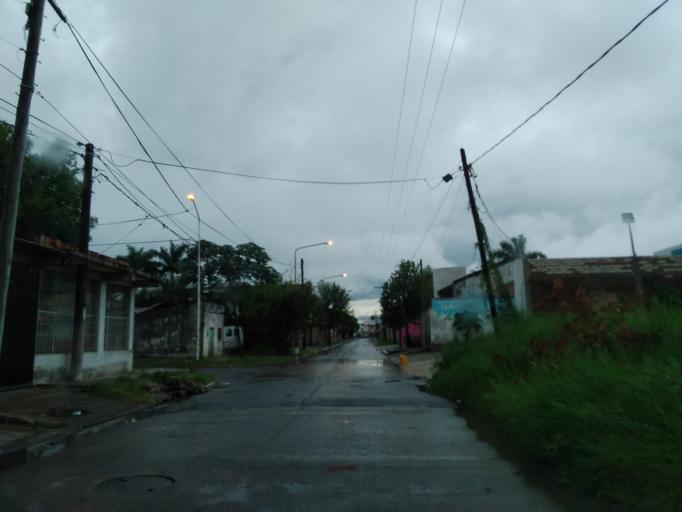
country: AR
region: Corrientes
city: Corrientes
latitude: -27.4933
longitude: -58.8201
